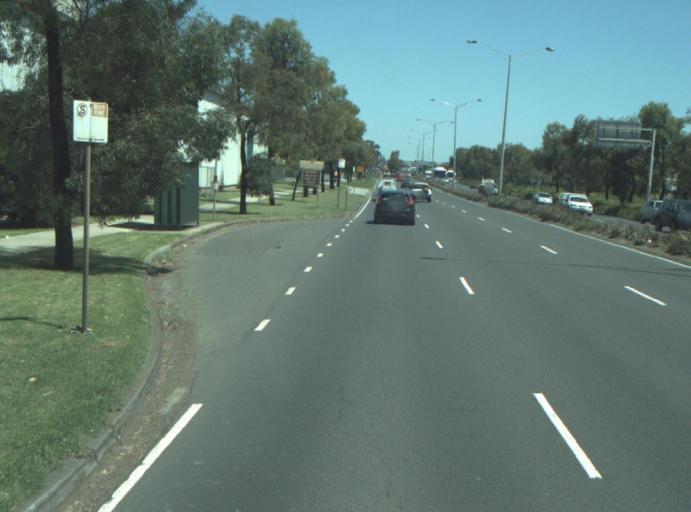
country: AU
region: Victoria
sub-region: Greater Geelong
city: Bell Park
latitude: -38.1155
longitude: 144.3545
